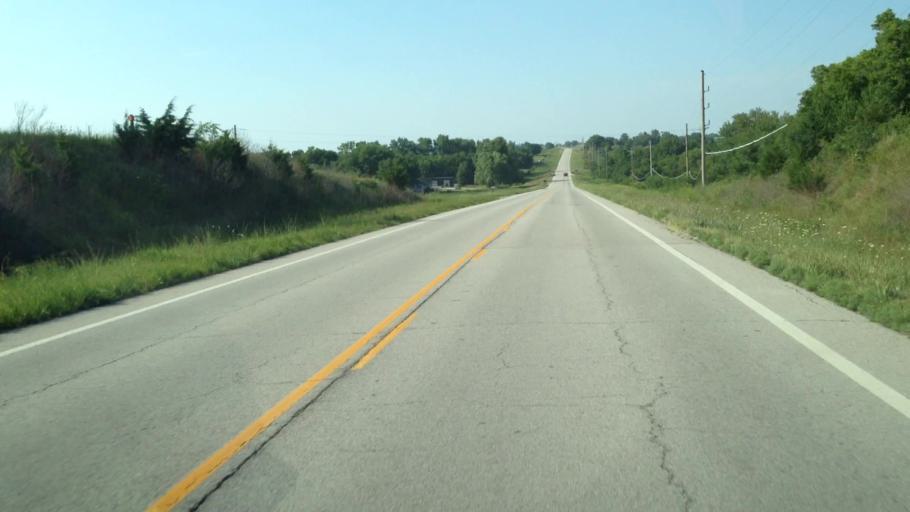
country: US
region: Kansas
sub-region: Allen County
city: Iola
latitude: 37.9891
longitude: -95.1705
